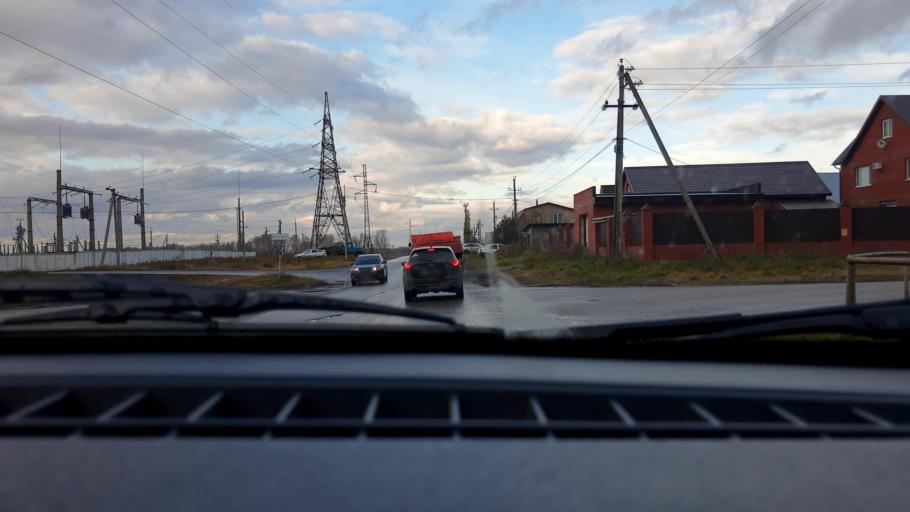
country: RU
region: Bashkortostan
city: Ufa
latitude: 54.8422
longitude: 55.9992
